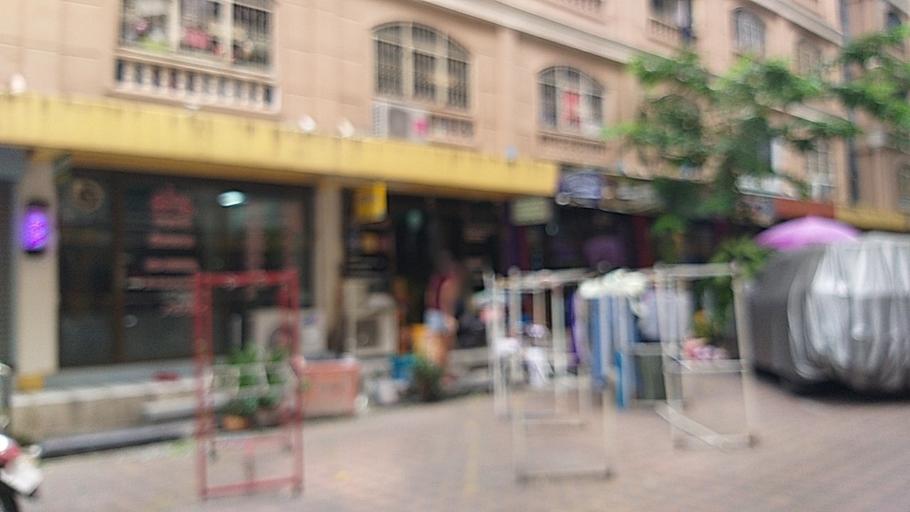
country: TH
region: Bangkok
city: Bang Na
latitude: 13.6718
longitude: 100.6813
